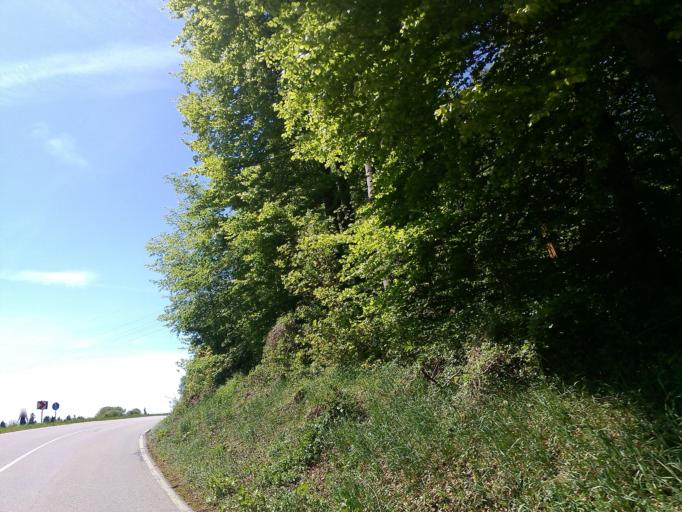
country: DE
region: Bavaria
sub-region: Upper Bavaria
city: Starnberg
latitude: 48.0234
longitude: 11.3589
